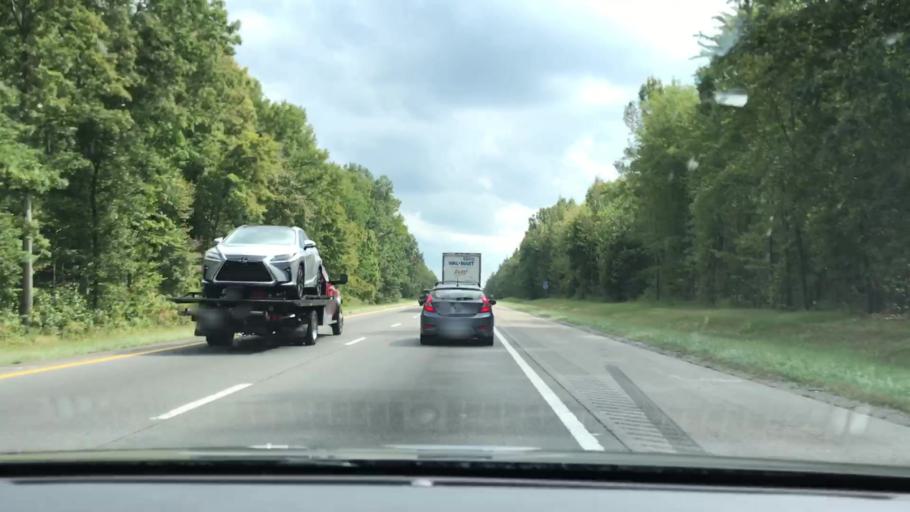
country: US
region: Tennessee
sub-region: Cheatham County
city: Pleasant View
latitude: 36.4445
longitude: -87.0915
